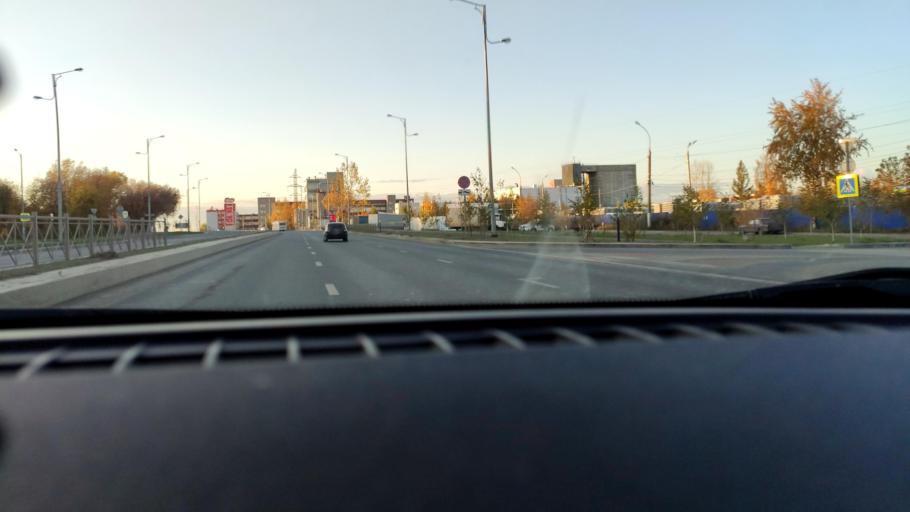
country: RU
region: Perm
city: Froly
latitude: 57.9509
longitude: 56.2643
